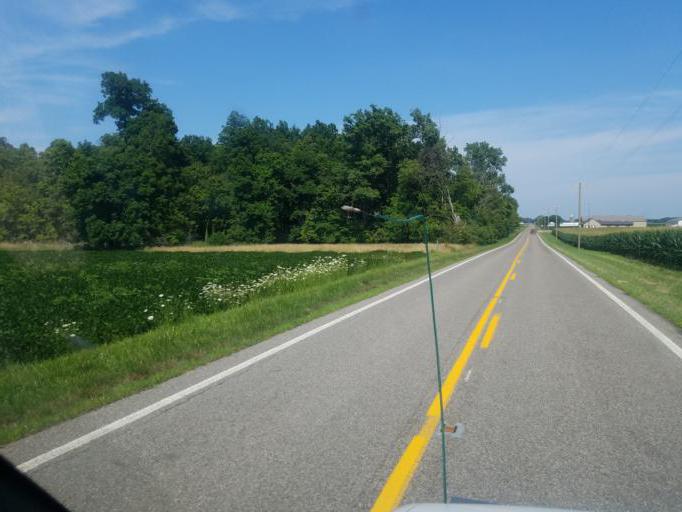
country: US
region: Ohio
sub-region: Shelby County
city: Jackson Center
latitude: 40.4977
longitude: -84.0394
